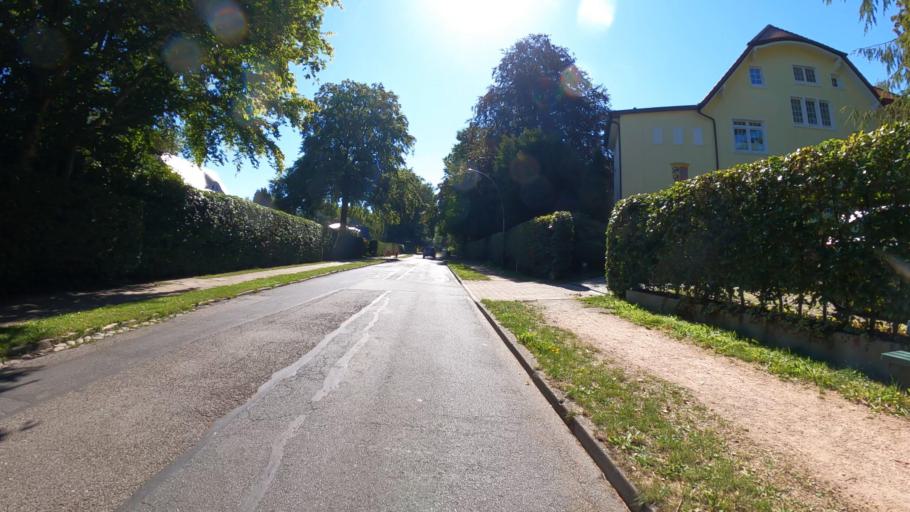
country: DE
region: Schleswig-Holstein
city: Aumuhle
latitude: 53.5245
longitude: 10.3165
